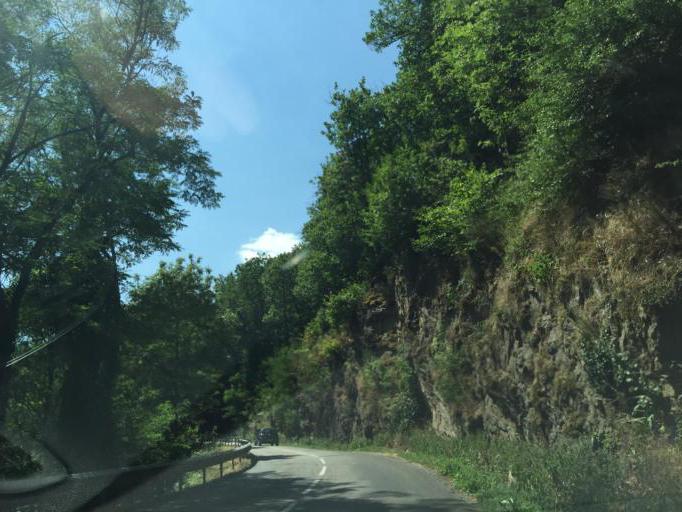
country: FR
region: Rhone-Alpes
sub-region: Departement de la Loire
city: Saint-Chamond
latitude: 45.4337
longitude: 4.5121
